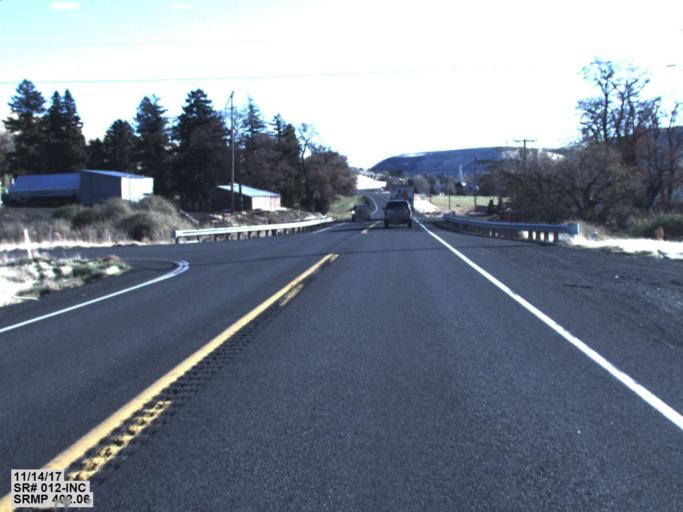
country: US
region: Washington
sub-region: Garfield County
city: Pomeroy
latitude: 46.4781
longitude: -117.6291
